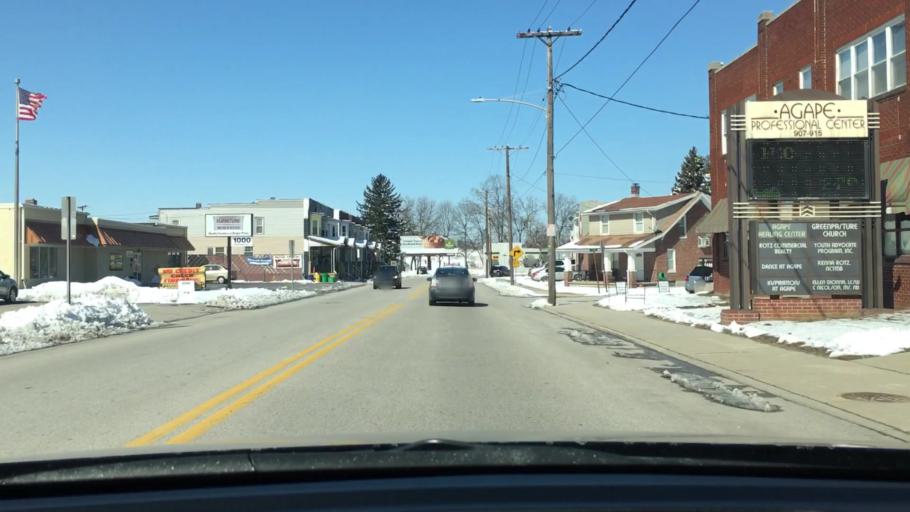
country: US
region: Pennsylvania
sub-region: York County
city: West York
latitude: 39.9674
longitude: -76.7501
